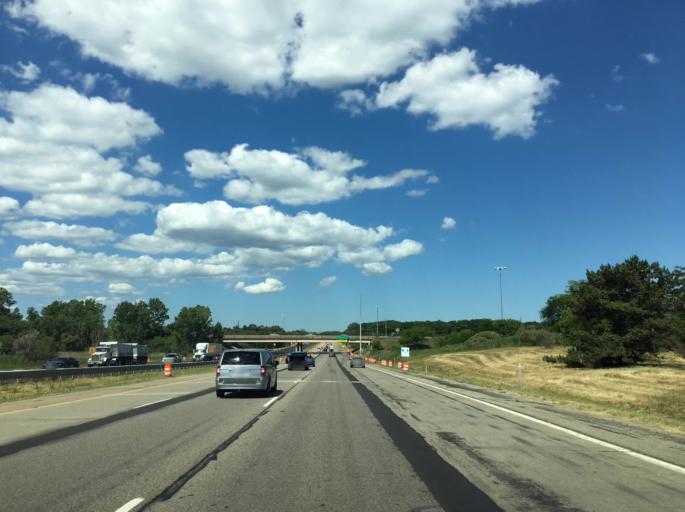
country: US
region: Michigan
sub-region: Oakland County
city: Pontiac
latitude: 42.7055
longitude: -83.3032
